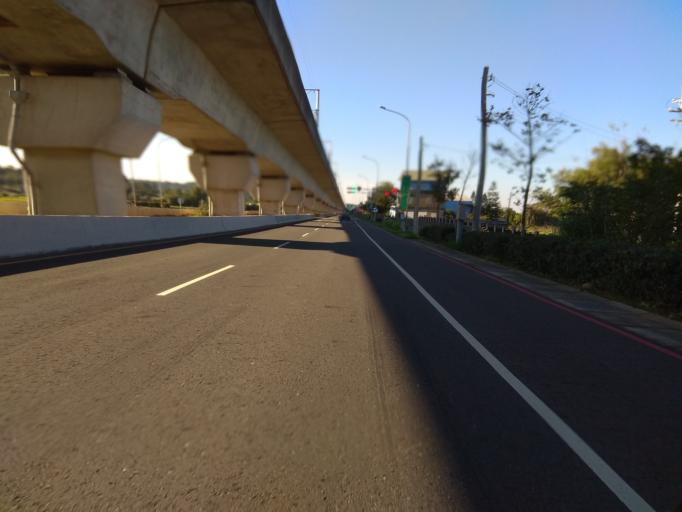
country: TW
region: Taiwan
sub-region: Hsinchu
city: Zhubei
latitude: 24.8986
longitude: 121.0804
